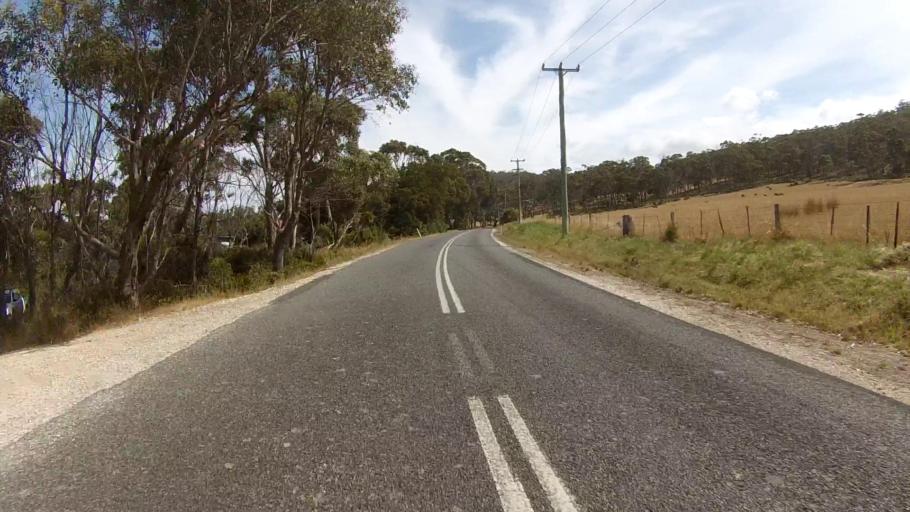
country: AU
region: Tasmania
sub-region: Huon Valley
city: Cygnet
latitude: -43.2780
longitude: 147.1631
